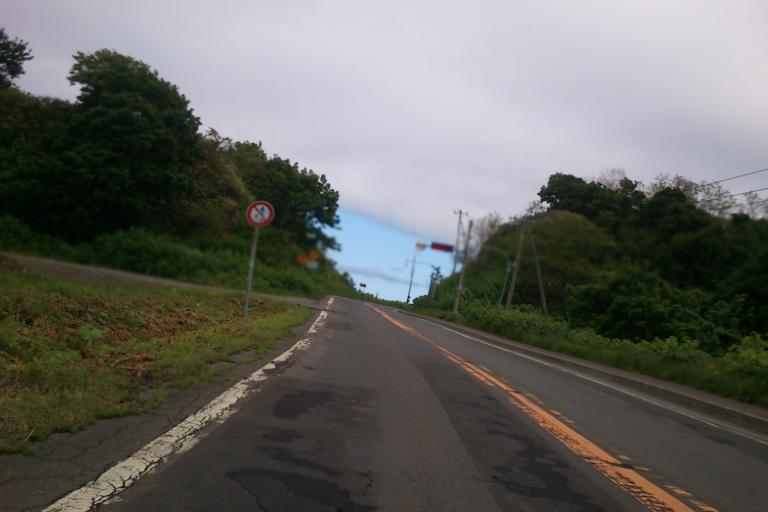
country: JP
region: Hokkaido
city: Ishikari
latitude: 43.4138
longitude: 141.4323
